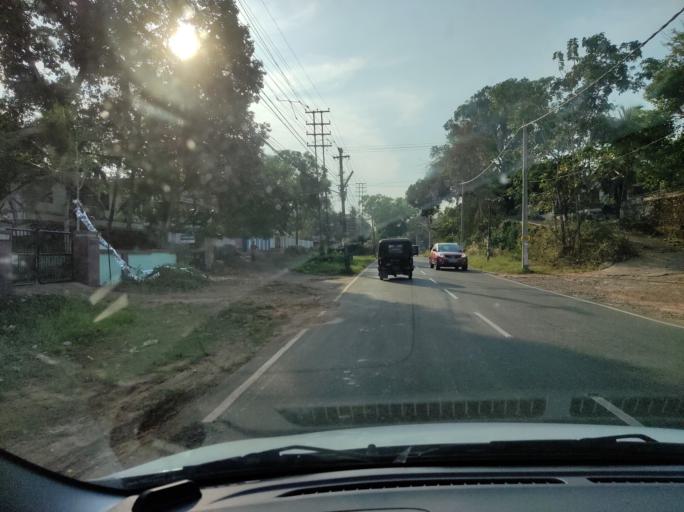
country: IN
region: Kerala
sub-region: Kottayam
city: Kottayam
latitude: 9.6297
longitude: 76.5322
